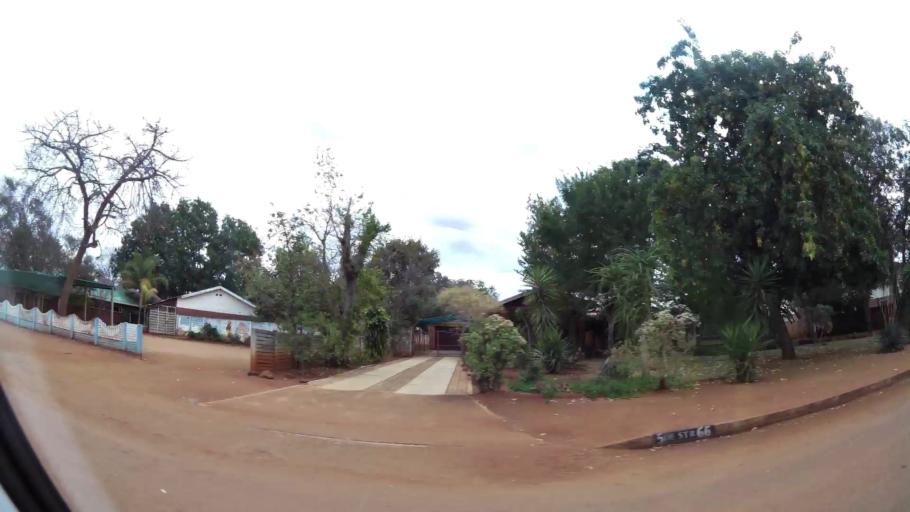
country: ZA
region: Limpopo
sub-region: Waterberg District Municipality
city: Modimolle
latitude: -24.5155
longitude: 28.7143
